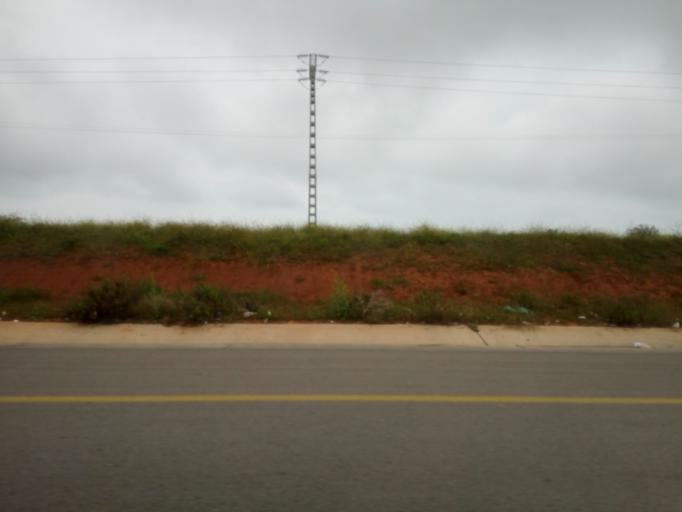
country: DZ
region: Tipaza
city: Bou Ismail
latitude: 36.5957
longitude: 2.6339
